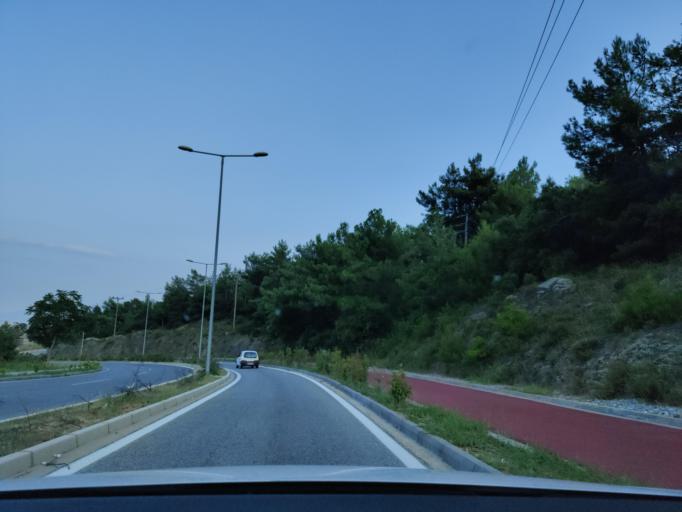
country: GR
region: East Macedonia and Thrace
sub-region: Nomos Kavalas
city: Kavala
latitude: 40.9388
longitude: 24.3802
